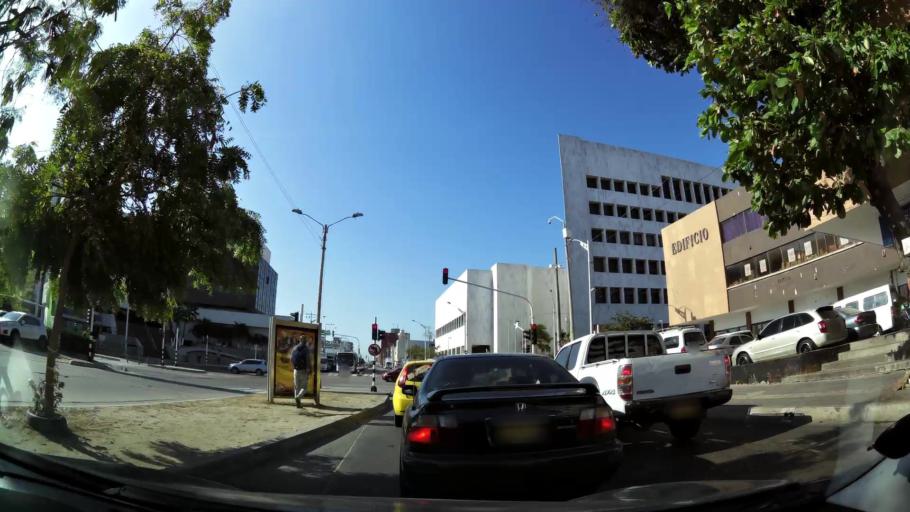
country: CO
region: Atlantico
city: Barranquilla
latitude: 10.9877
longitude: -74.7848
